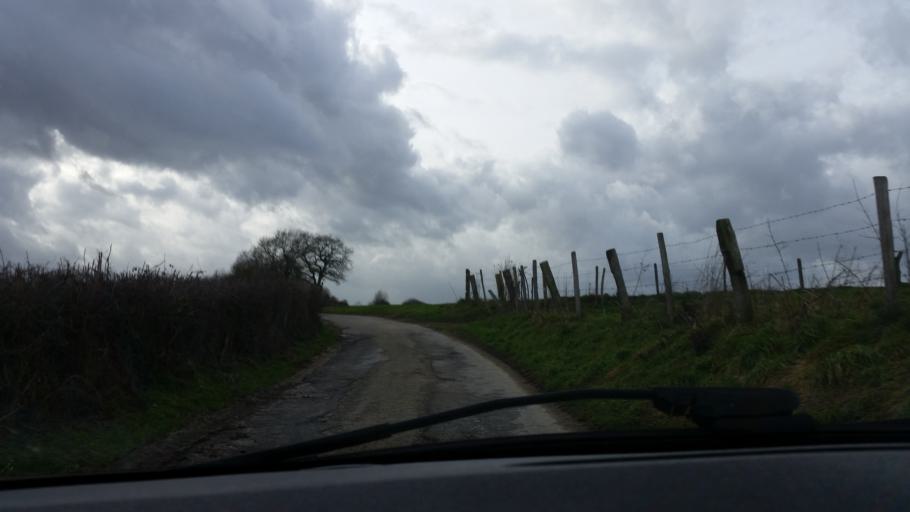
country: FR
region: Nord-Pas-de-Calais
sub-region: Departement du Nord
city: Jeumont
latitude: 50.2386
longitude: 4.1214
